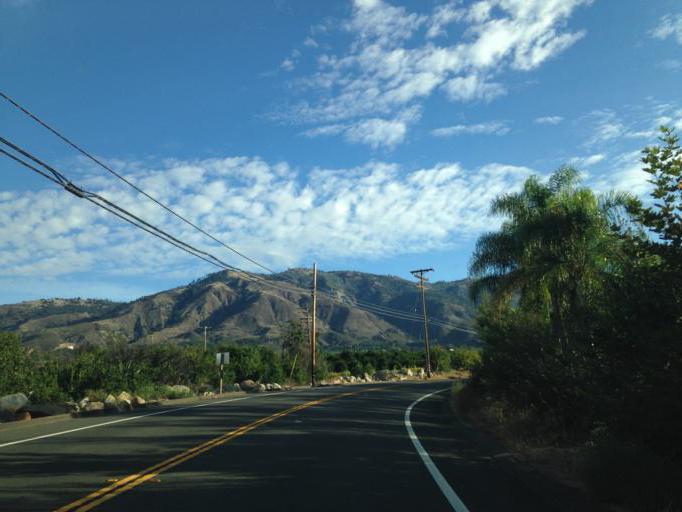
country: US
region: California
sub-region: San Diego County
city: Valley Center
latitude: 33.2947
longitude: -116.9464
